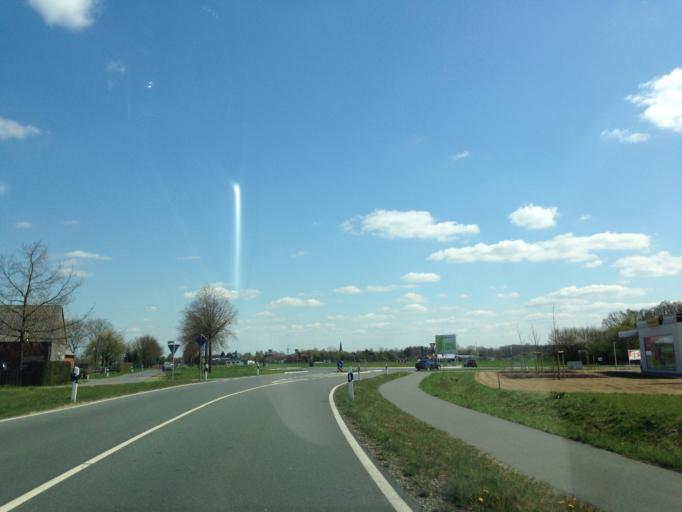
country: DE
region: North Rhine-Westphalia
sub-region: Regierungsbezirk Munster
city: Muenster
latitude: 51.8933
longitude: 7.5838
